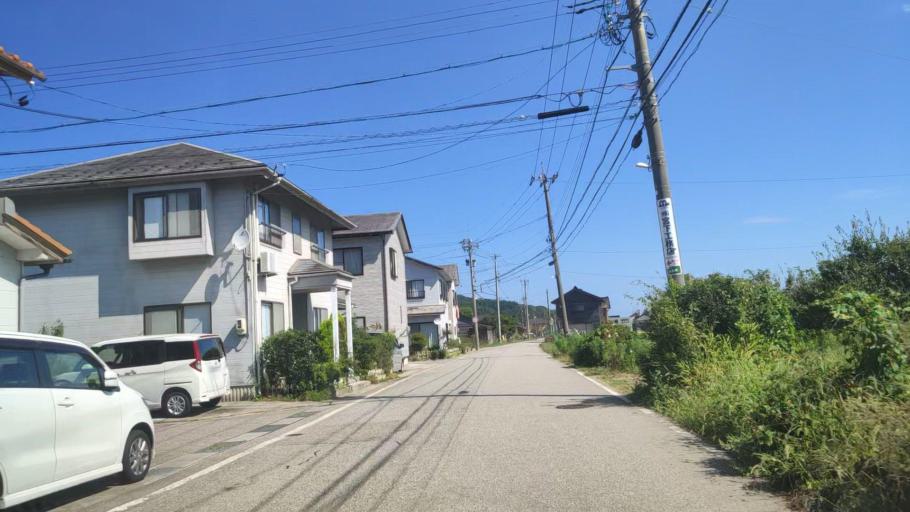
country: JP
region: Ishikawa
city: Nanao
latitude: 37.3747
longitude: 136.8755
